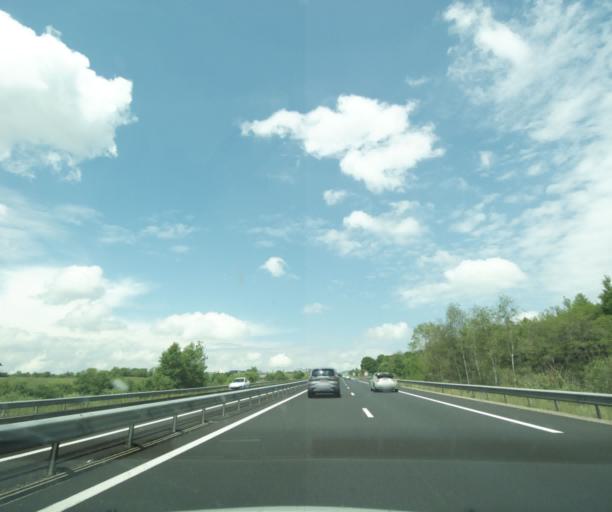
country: FR
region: Auvergne
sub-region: Departement du Cantal
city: Saint-Flour
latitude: 45.0531
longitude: 3.1111
